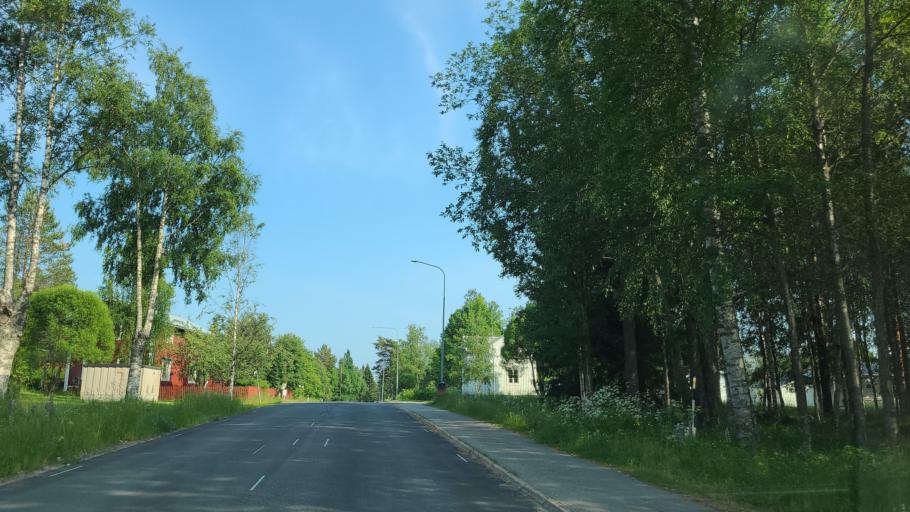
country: SE
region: Vaesterbotten
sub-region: Skelleftea Kommun
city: Burea
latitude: 64.3662
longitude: 21.3256
